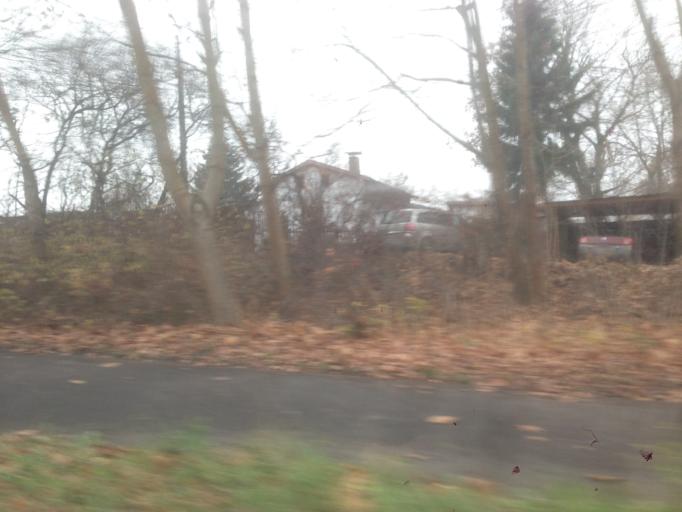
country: DE
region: Berlin
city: Blankenfelde
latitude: 52.6344
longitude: 13.3801
